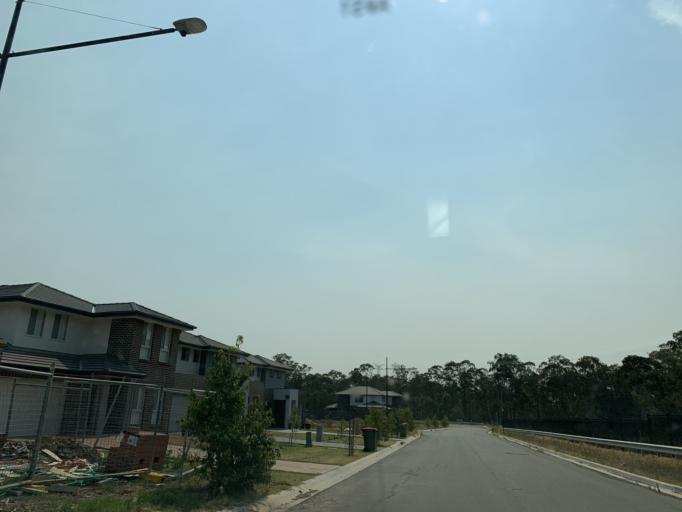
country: AU
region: New South Wales
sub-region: Blacktown
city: Blackett
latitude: -33.7121
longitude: 150.8175
